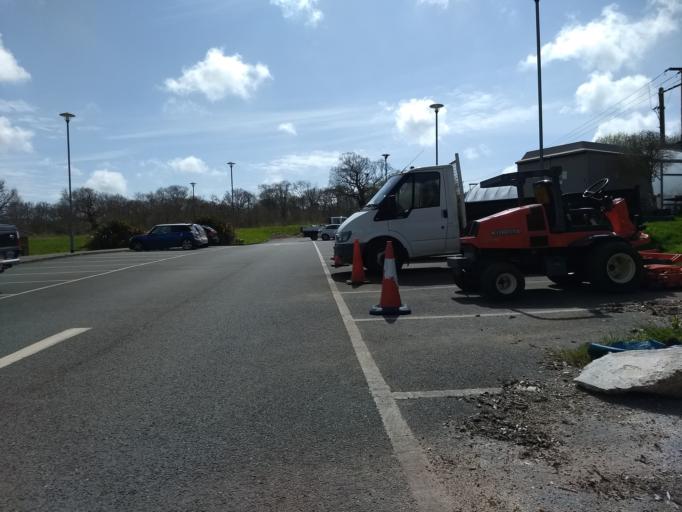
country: GB
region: England
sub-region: Isle of Wight
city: Newchurch
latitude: 50.7230
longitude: -1.2284
